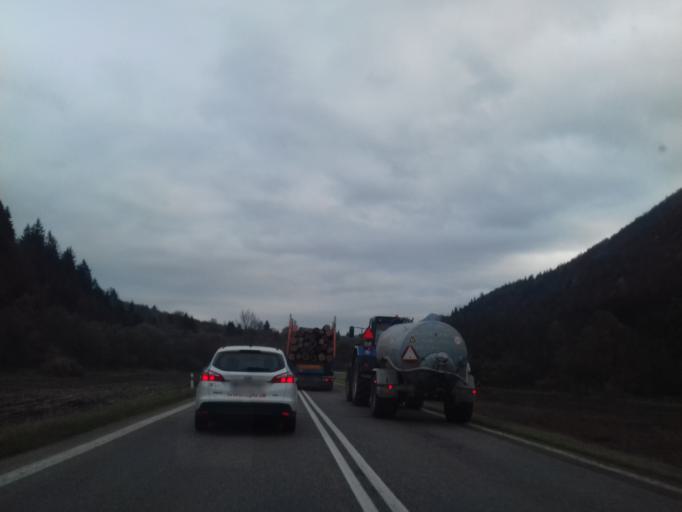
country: SK
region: Zilinsky
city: Ruzomberok
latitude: 48.9782
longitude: 19.2750
